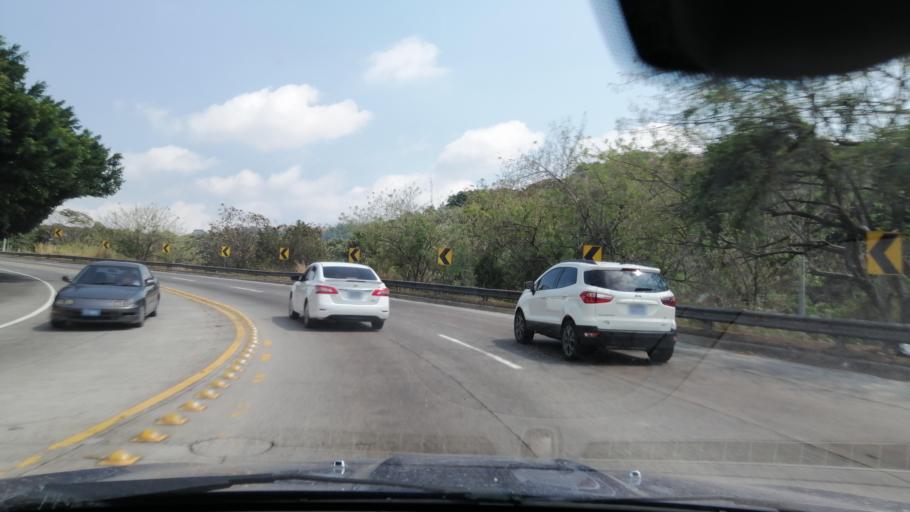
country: SV
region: La Libertad
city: Santa Tecla
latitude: 13.6759
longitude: -89.3054
